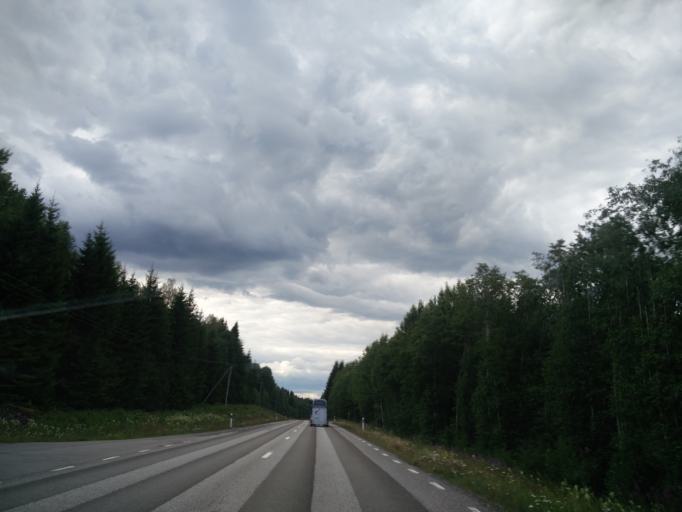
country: SE
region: OErebro
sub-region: Hallefors Kommun
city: Haellefors
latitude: 59.7716
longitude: 14.3978
